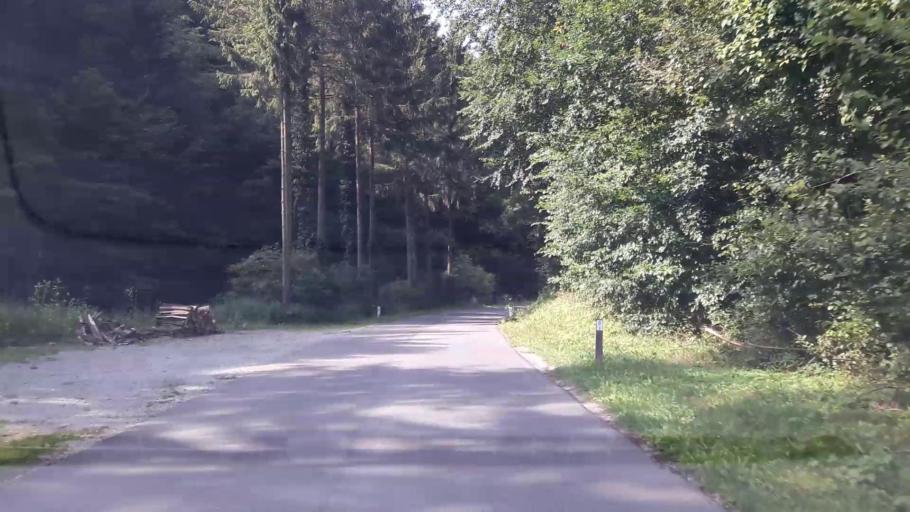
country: AT
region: Lower Austria
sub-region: Politischer Bezirk Krems
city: Aggsbach
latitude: 48.2930
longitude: 15.3949
